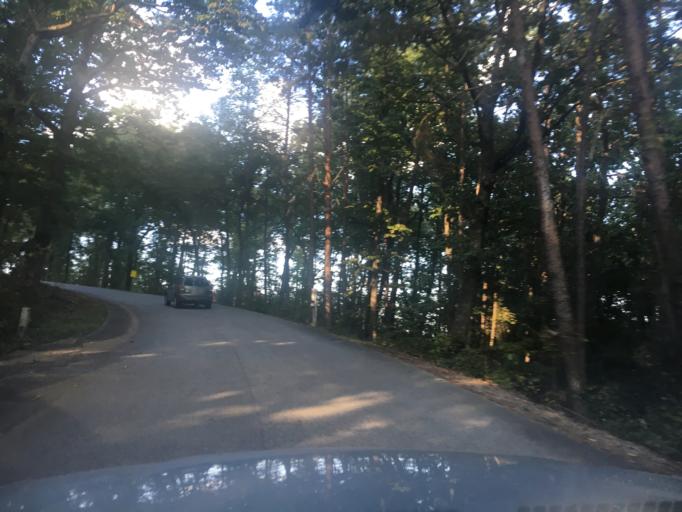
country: US
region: South Carolina
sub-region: Greenville County
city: Mauldin
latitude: 34.8391
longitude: -82.3071
